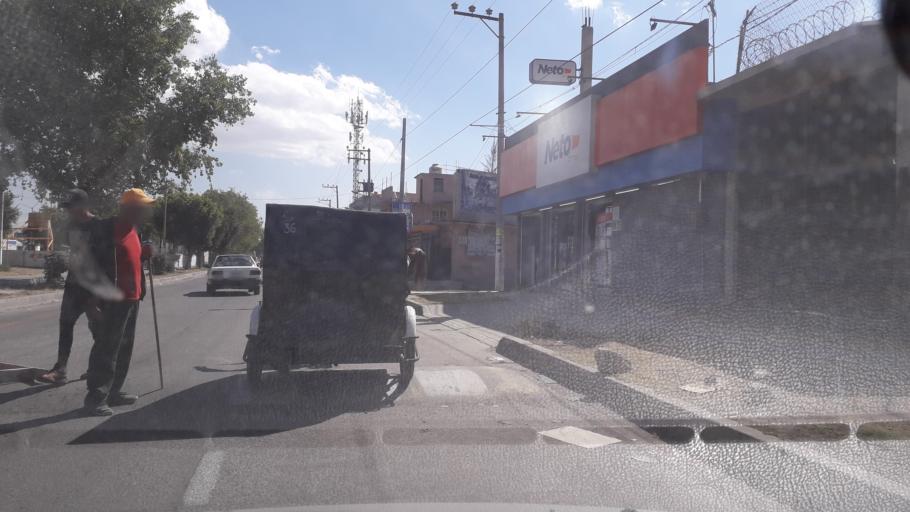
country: MX
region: Mexico
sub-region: Jaltenco
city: Alborada Jaltenco
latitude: 19.6567
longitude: -99.0684
